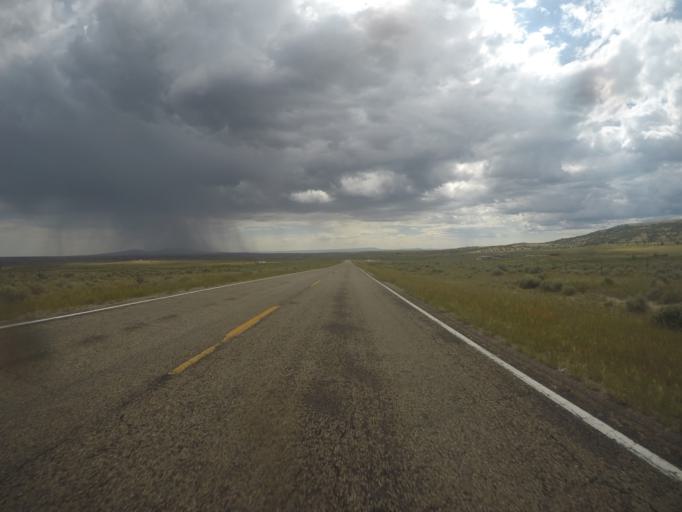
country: US
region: Utah
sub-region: Daggett County
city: Manila
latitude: 41.0260
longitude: -109.8879
